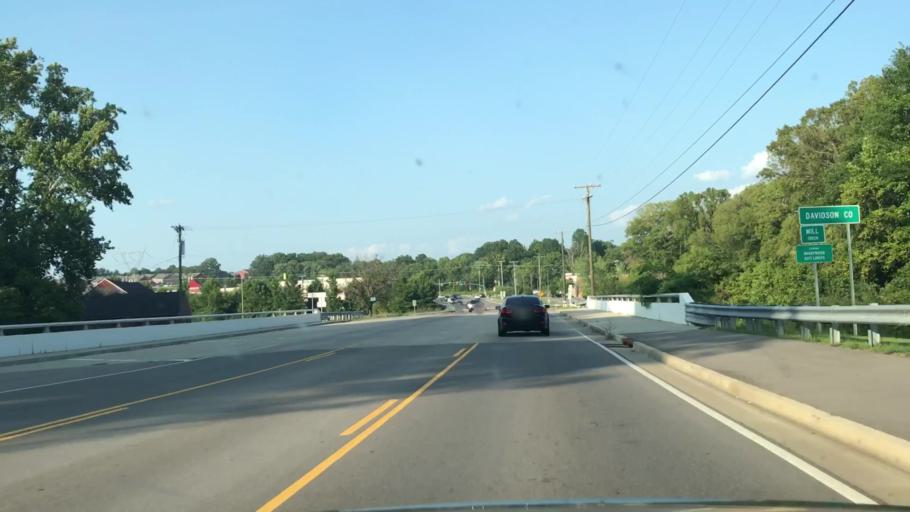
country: US
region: Tennessee
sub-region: Williamson County
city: Nolensville
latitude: 35.9944
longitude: -86.6926
